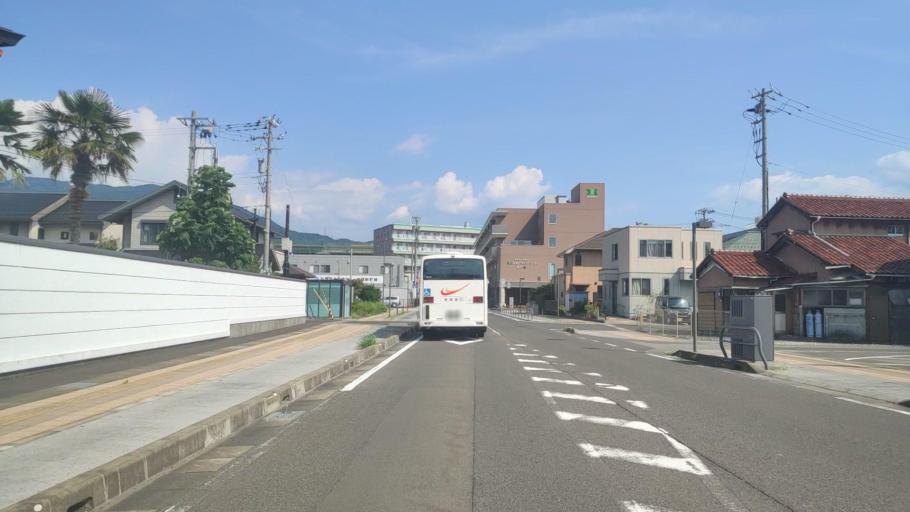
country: JP
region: Fukui
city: Tsuruga
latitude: 35.6444
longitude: 136.0723
